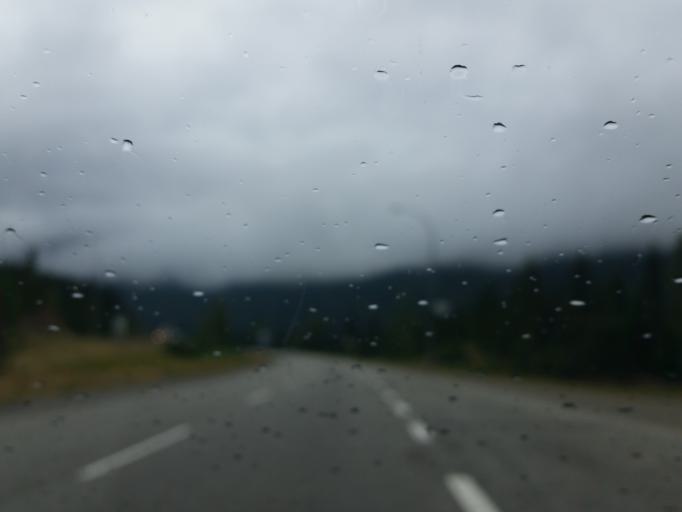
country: CA
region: British Columbia
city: Hope
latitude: 49.6334
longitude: -121.0101
